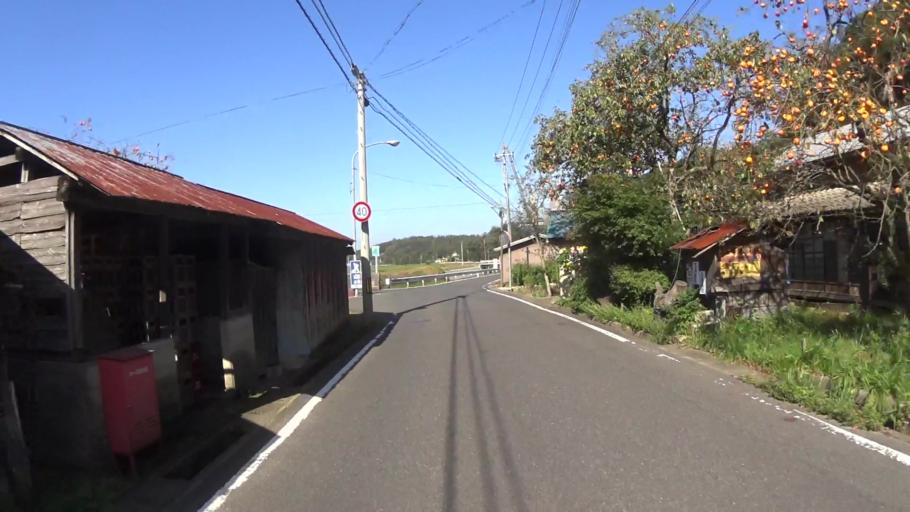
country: JP
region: Kyoto
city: Miyazu
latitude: 35.6569
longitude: 135.1130
